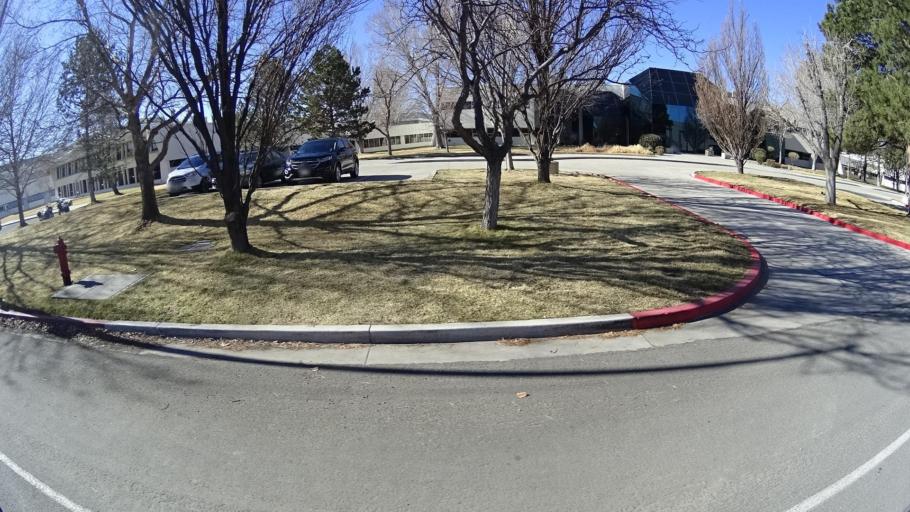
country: US
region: Nevada
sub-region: Washoe County
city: Sparks
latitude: 39.5054
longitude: -119.7584
